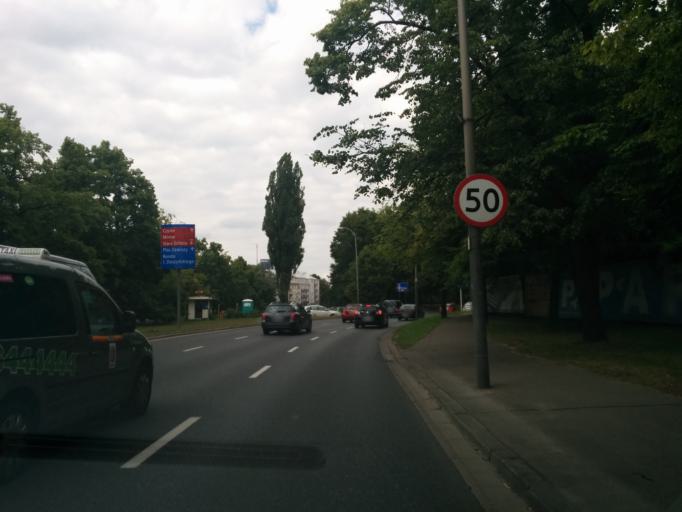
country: PL
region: Masovian Voivodeship
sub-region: Warszawa
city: Ochota
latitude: 52.2142
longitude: 20.9888
